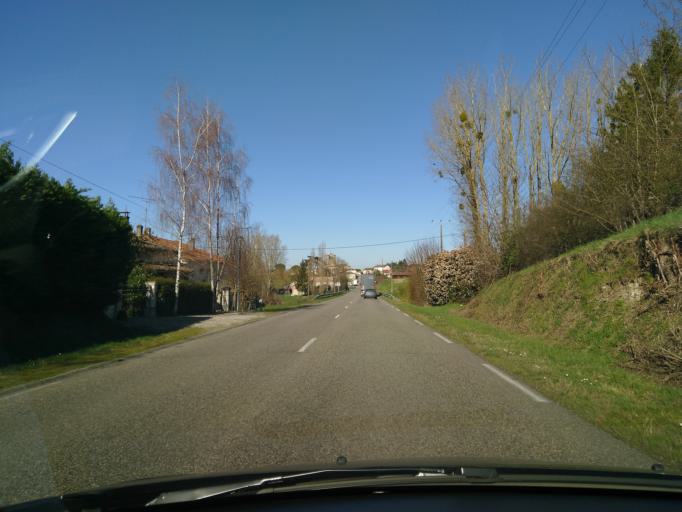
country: FR
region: Aquitaine
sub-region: Departement du Lot-et-Garonne
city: Cancon
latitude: 44.5785
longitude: 0.6248
